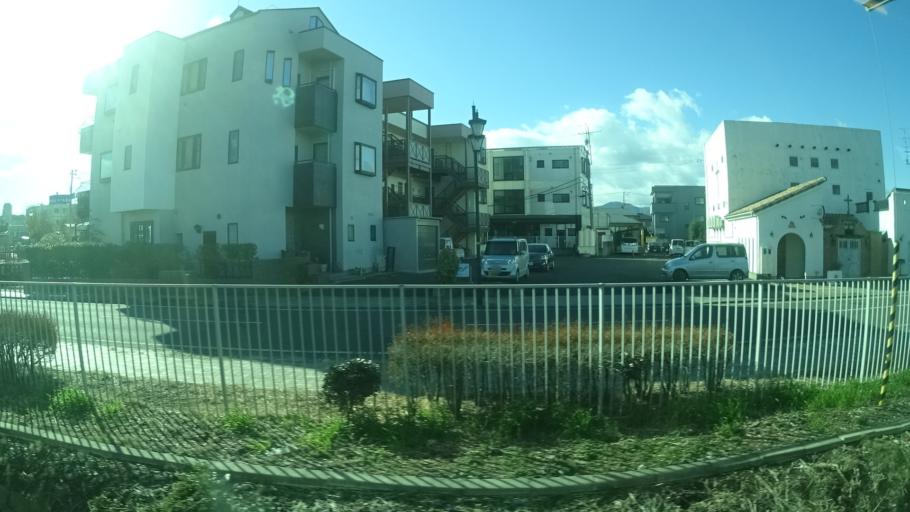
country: JP
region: Fukushima
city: Namie
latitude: 37.6394
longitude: 140.9697
